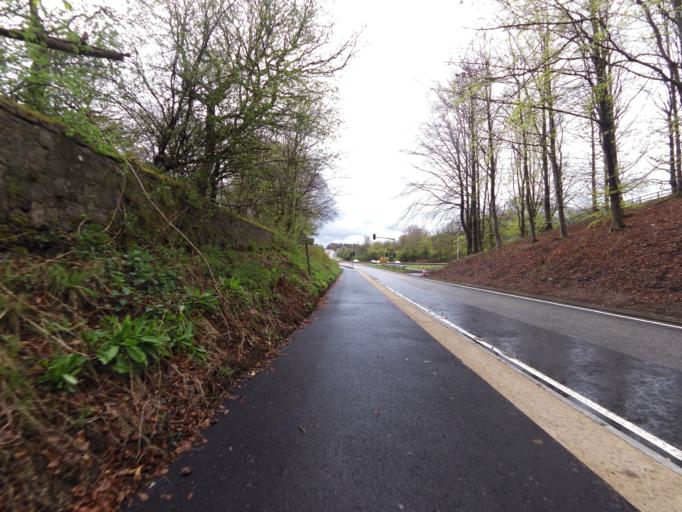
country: GB
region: Scotland
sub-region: Edinburgh
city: Queensferry
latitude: 55.9798
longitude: -3.3470
